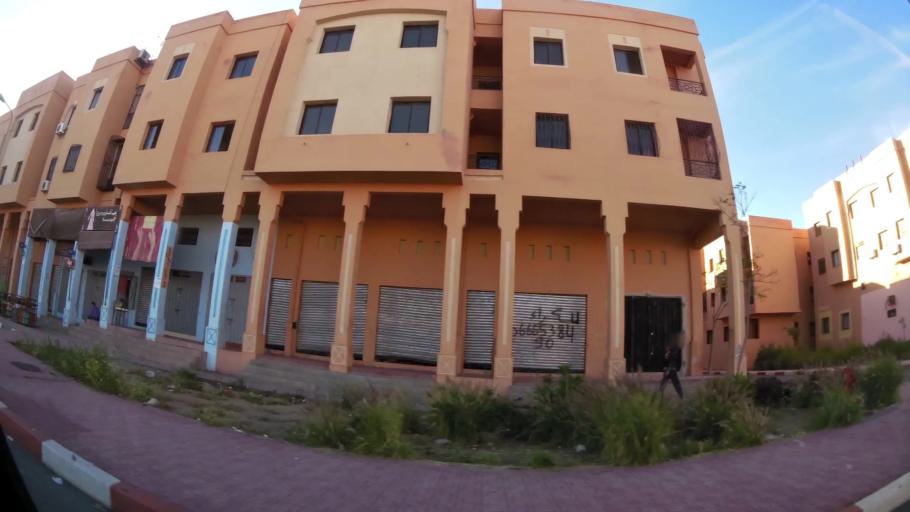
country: MA
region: Marrakech-Tensift-Al Haouz
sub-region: Marrakech
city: Marrakesh
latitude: 31.7638
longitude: -8.1113
